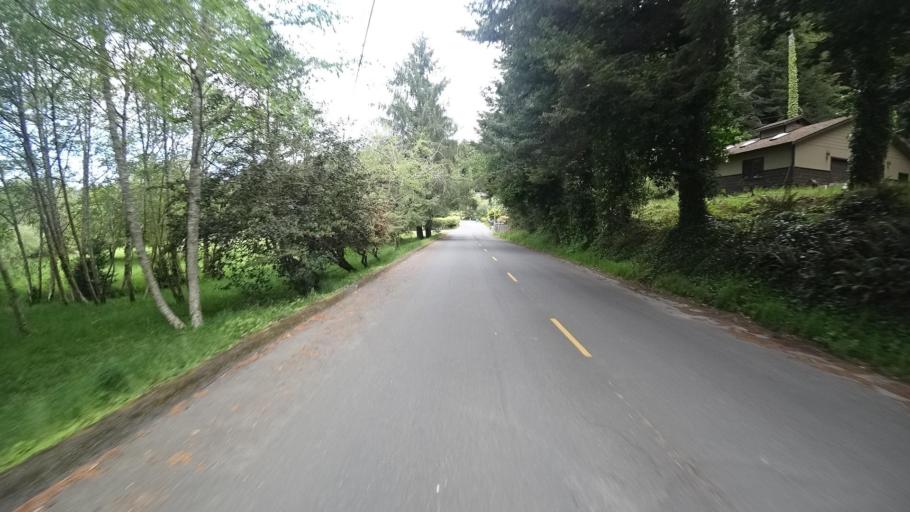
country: US
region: California
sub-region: Humboldt County
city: Bayside
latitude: 40.8550
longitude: -124.0569
